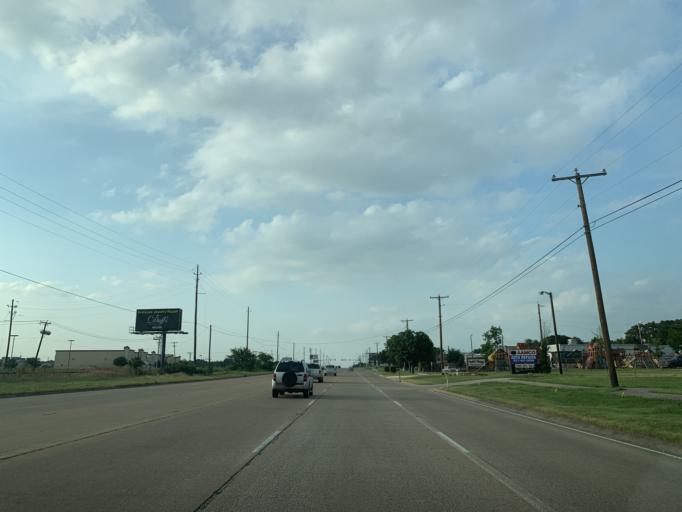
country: US
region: Texas
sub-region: Tarrant County
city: Keller
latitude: 32.9076
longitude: -97.2565
